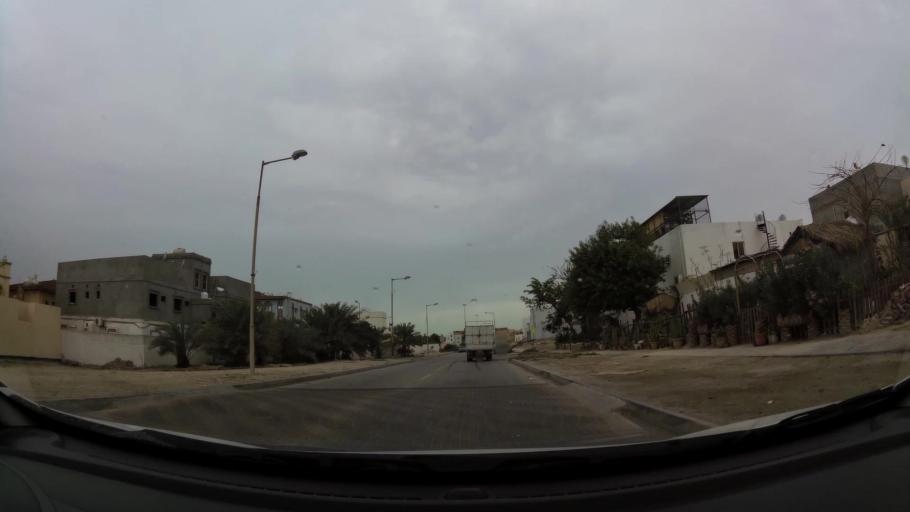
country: BH
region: Central Governorate
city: Madinat Hamad
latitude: 26.1017
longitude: 50.5018
